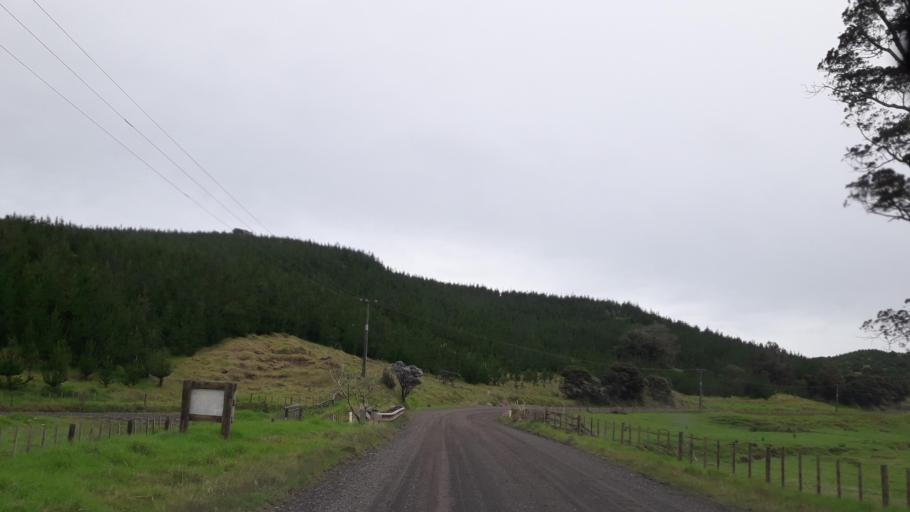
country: NZ
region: Northland
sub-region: Far North District
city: Ahipara
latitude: -35.4348
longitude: 173.3417
